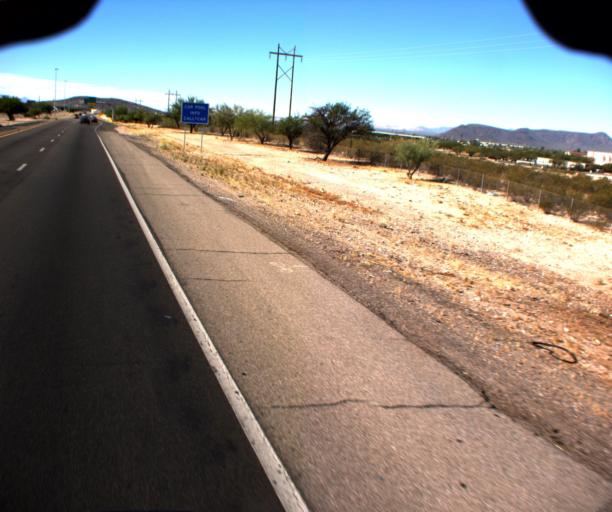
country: US
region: Arizona
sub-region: Pima County
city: Drexel Heights
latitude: 32.1476
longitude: -110.9868
